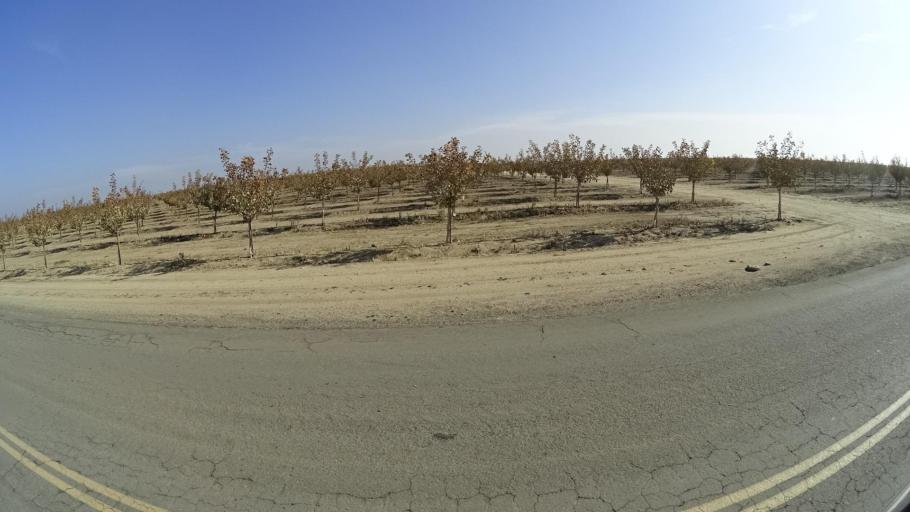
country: US
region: California
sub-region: Kern County
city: McFarland
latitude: 35.6205
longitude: -119.1688
